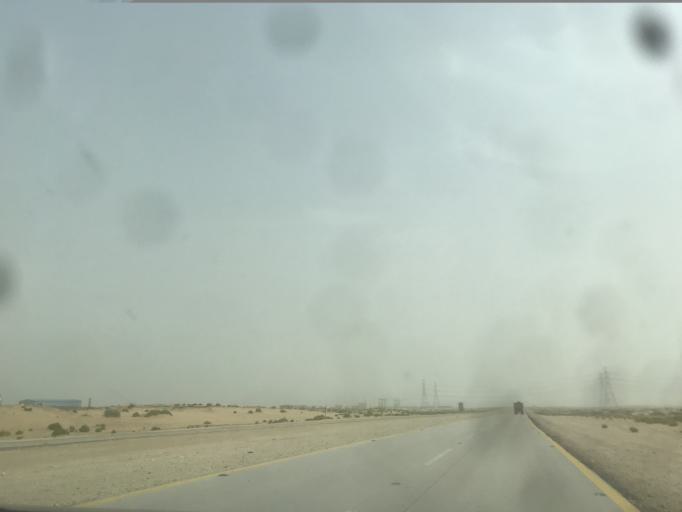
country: SA
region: Eastern Province
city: Abqaiq
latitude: 25.9101
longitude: 49.9476
